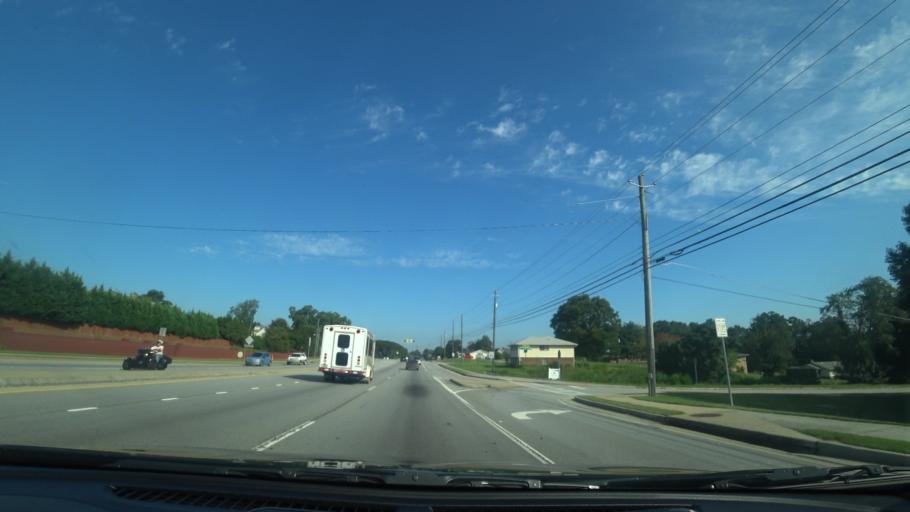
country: US
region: Georgia
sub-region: Gwinnett County
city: Grayson
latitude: 33.9005
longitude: -83.9620
